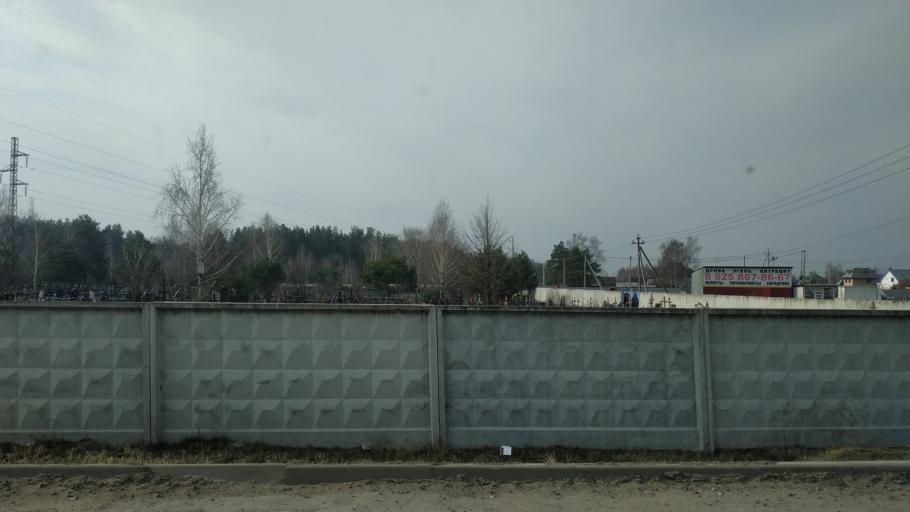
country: RU
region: Moskovskaya
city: Malyshevo
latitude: 55.4938
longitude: 38.3651
